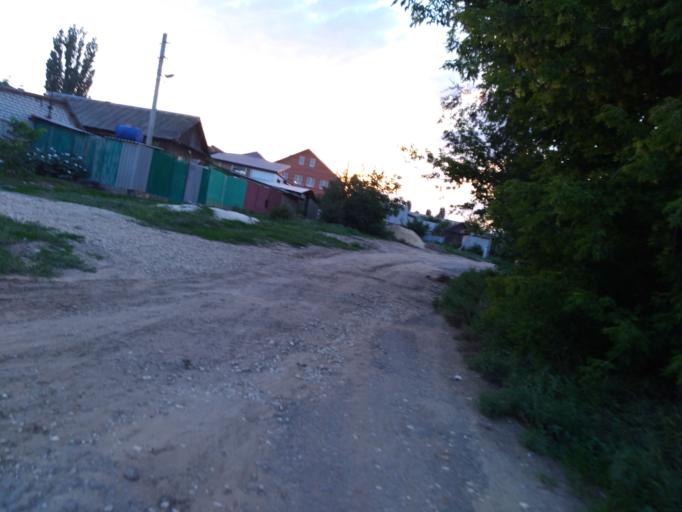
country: RU
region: Volgograd
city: Volgograd
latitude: 48.6692
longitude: 44.4531
